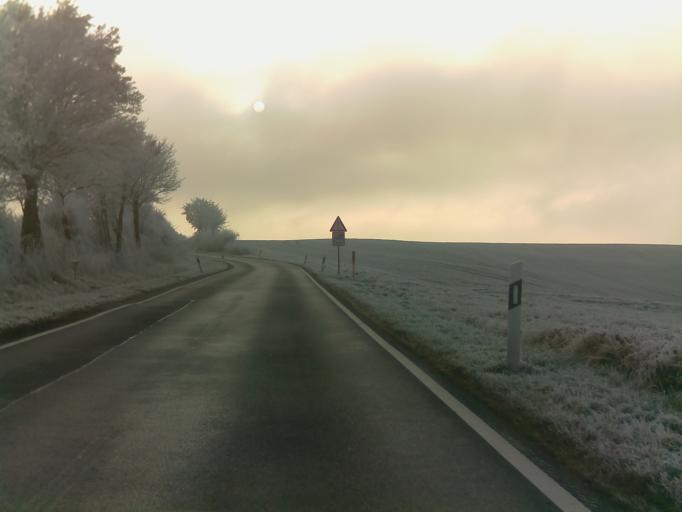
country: DE
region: Hesse
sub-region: Regierungsbezirk Darmstadt
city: Rossdorf
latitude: 49.8423
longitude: 8.7681
